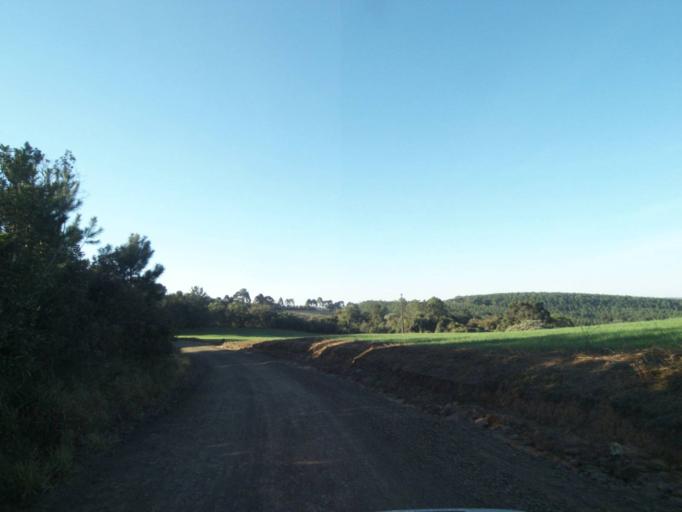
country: BR
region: Parana
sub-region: Telemaco Borba
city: Telemaco Borba
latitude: -24.4301
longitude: -50.5971
